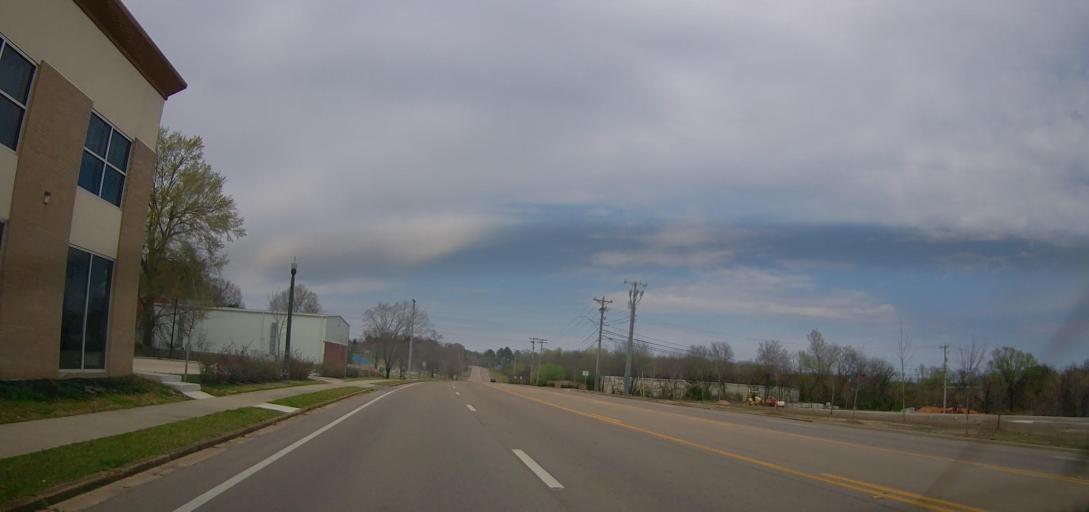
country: US
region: Mississippi
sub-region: Lee County
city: Tupelo
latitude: 34.2632
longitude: -88.7037
